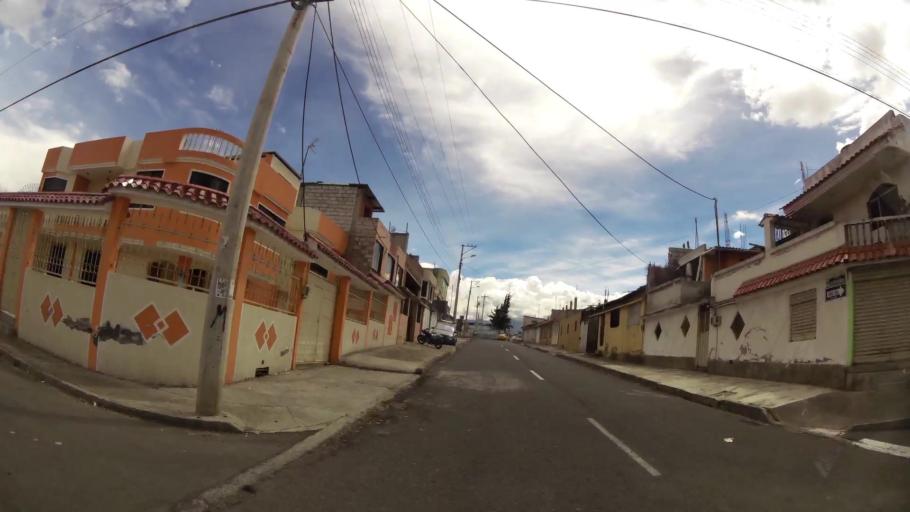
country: EC
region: Tungurahua
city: Ambato
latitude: -1.2623
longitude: -78.6102
